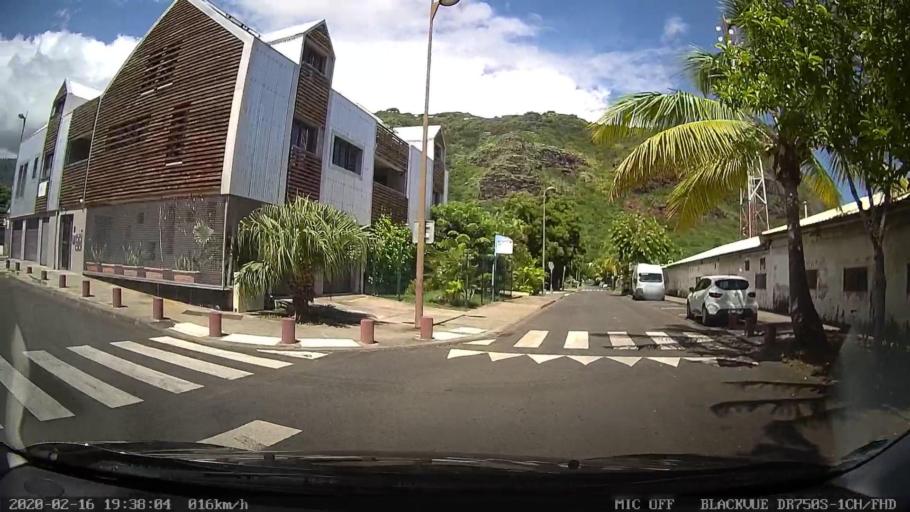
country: RE
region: Reunion
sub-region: Reunion
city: Saint-Denis
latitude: -20.8792
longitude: 55.4418
